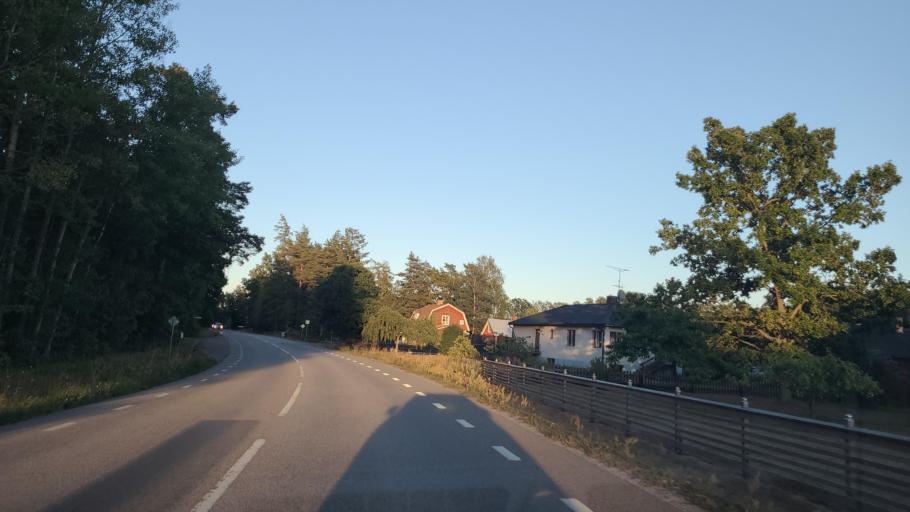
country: SE
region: Kalmar
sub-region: Borgholms Kommun
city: Borgholm
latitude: 57.2592
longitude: 17.0394
